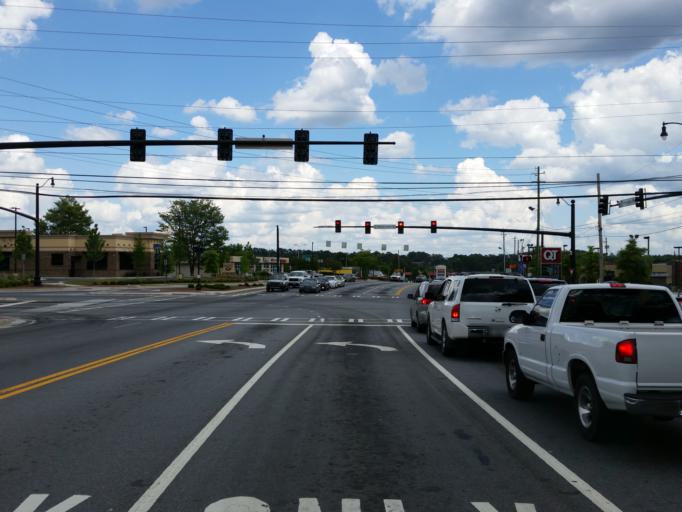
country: US
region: Georgia
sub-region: Cobb County
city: Marietta
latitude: 33.9434
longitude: -84.5356
